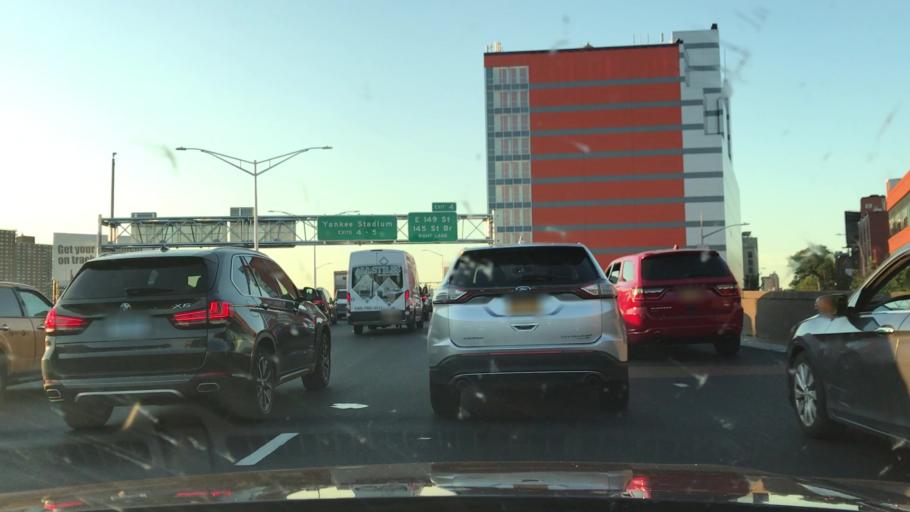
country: US
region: New Jersey
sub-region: Bergen County
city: Edgewater
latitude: 40.8153
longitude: -73.9307
